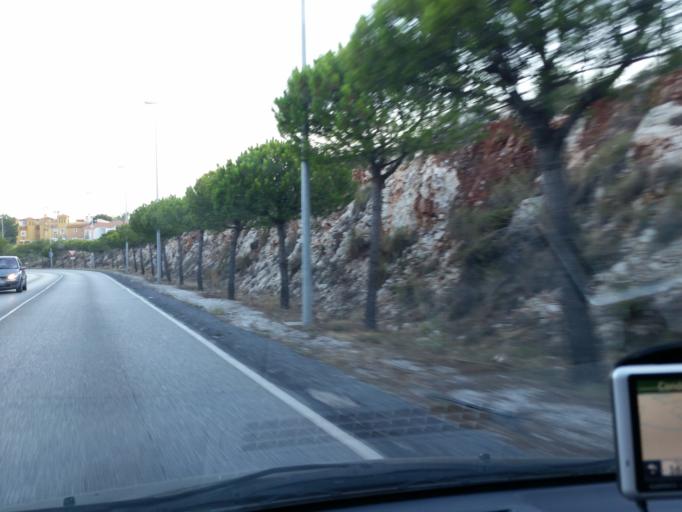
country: ES
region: Andalusia
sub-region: Provincia de Malaga
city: Torremolinos
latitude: 36.6090
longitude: -4.5346
